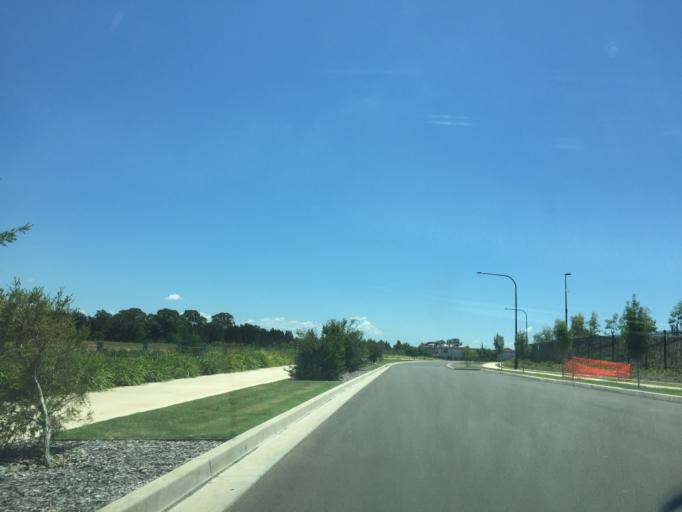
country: AU
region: New South Wales
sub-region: Blacktown
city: Doonside
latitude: -33.7946
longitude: 150.8635
